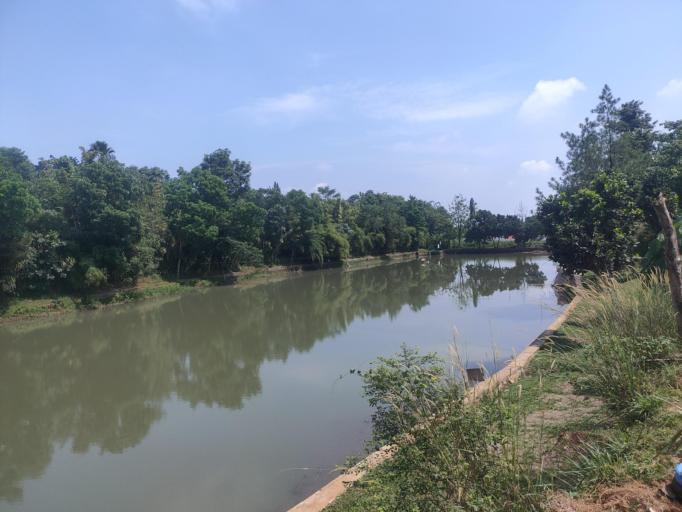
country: ID
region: West Java
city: Ciampea
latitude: -6.5257
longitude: 106.7003
